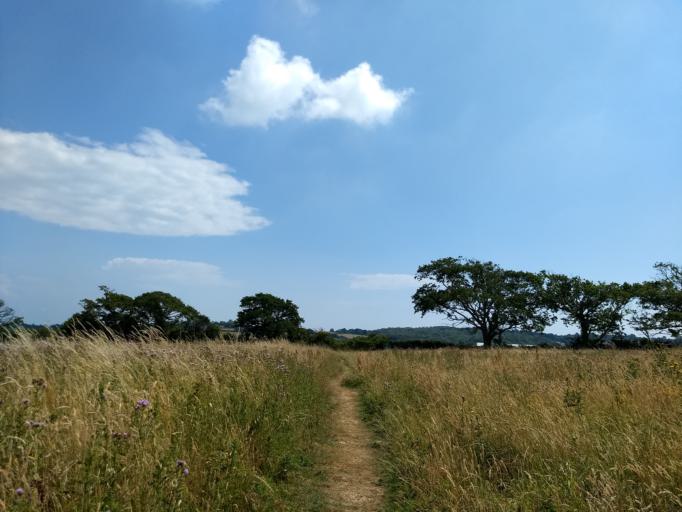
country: GB
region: England
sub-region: Isle of Wight
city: Bembridge
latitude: 50.6810
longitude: -1.1139
